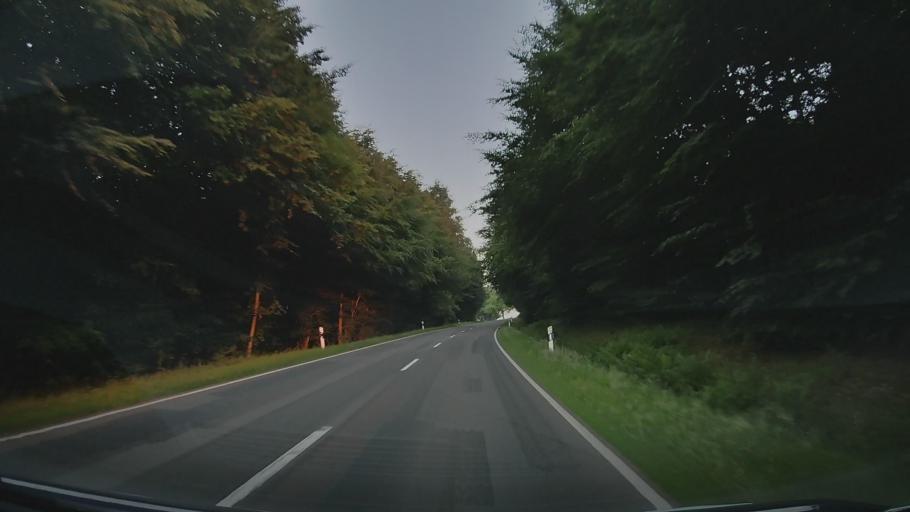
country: DE
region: Lower Saxony
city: Aerzen
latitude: 52.0236
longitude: 9.2863
